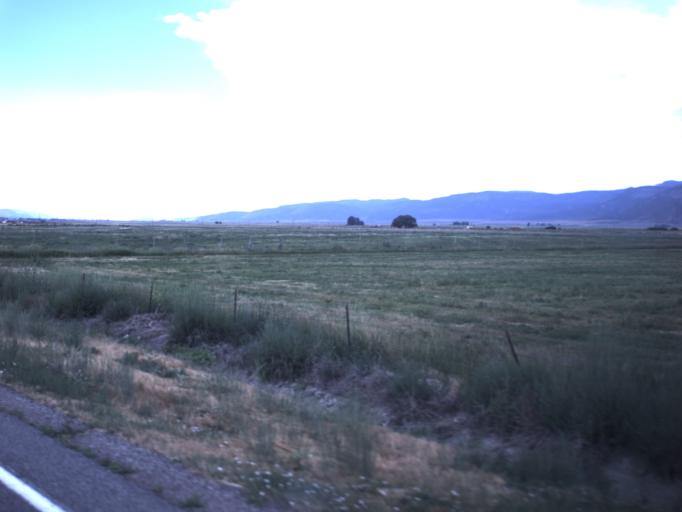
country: US
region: Utah
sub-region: Sanpete County
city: Moroni
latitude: 39.4695
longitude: -111.5628
